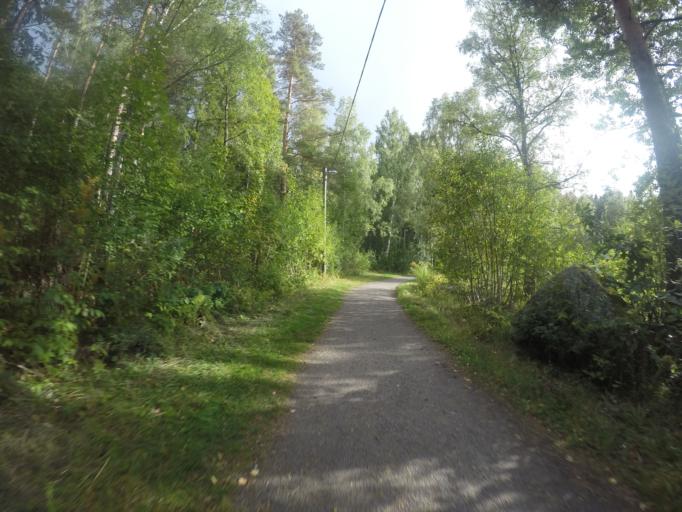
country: SE
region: Vaestmanland
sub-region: Vasteras
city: Vasteras
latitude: 59.6510
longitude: 16.5169
